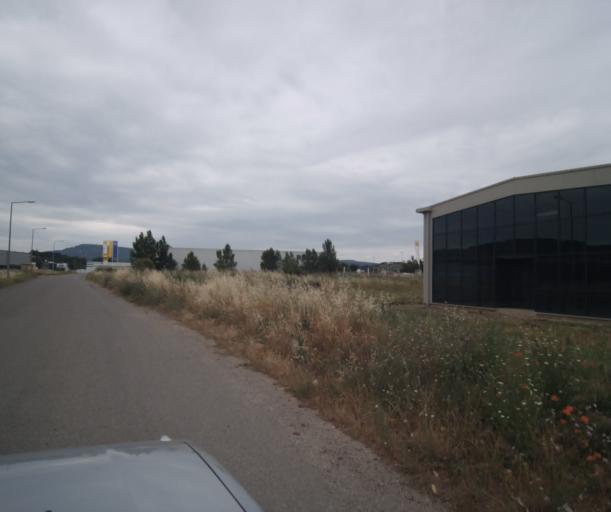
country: FR
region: Languedoc-Roussillon
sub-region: Departement de l'Aude
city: Limoux
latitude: 43.0767
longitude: 2.2233
